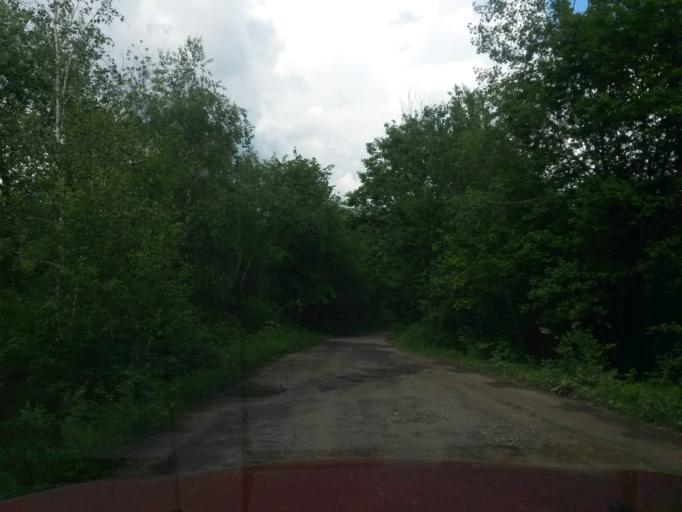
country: UA
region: Zakarpattia
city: Velykyi Bereznyi
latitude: 48.9006
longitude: 22.5173
